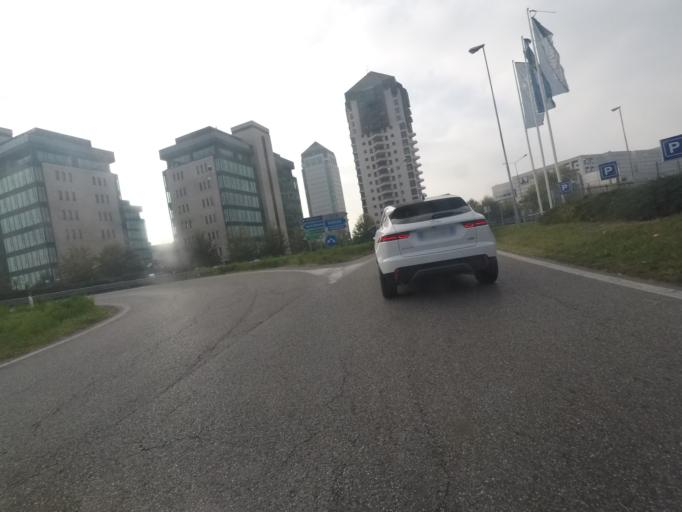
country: IT
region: Lombardy
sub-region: Provincia di Monza e Brianza
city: Vimercate
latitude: 45.6028
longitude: 9.3607
